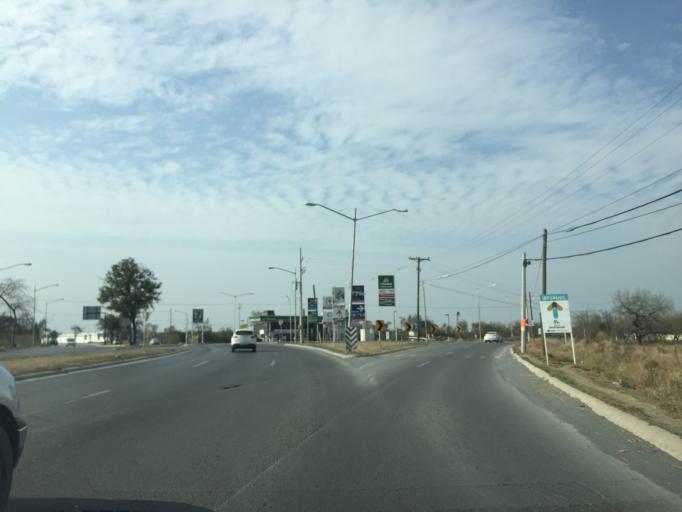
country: MX
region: Nuevo Leon
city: Apodaca
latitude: 25.7723
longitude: -100.2004
